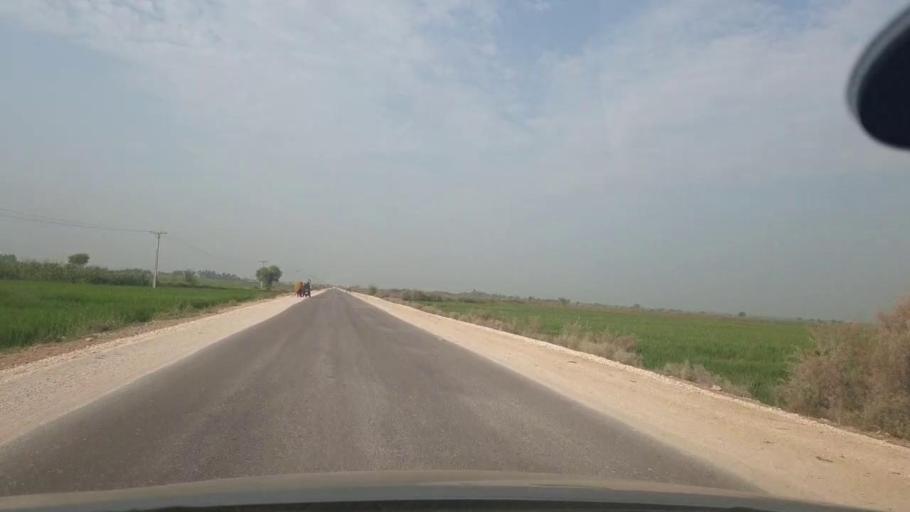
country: PK
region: Sindh
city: Jacobabad
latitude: 28.1481
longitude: 68.3484
